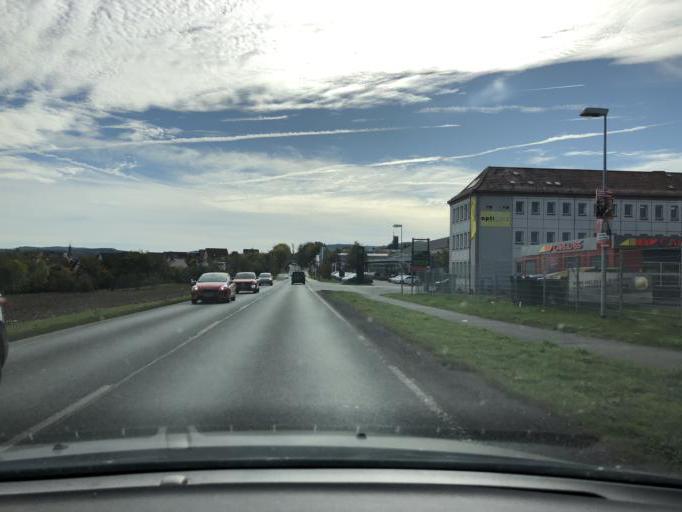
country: DE
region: Thuringia
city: Saalfeld
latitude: 50.6568
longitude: 11.3493
